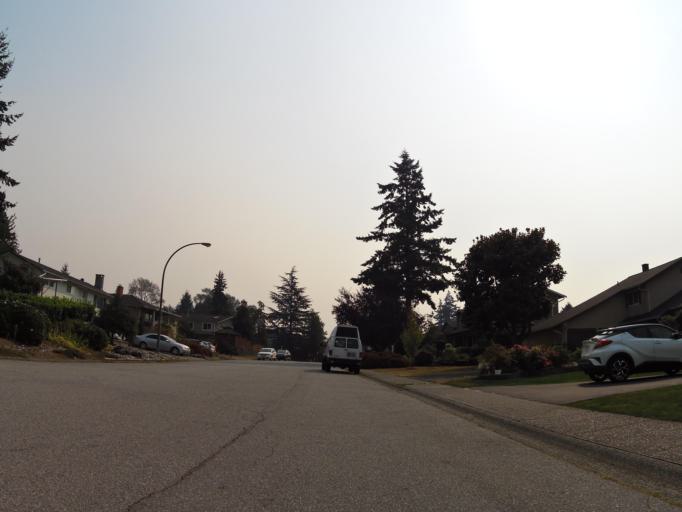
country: CA
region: British Columbia
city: Delta
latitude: 49.1494
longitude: -122.9265
